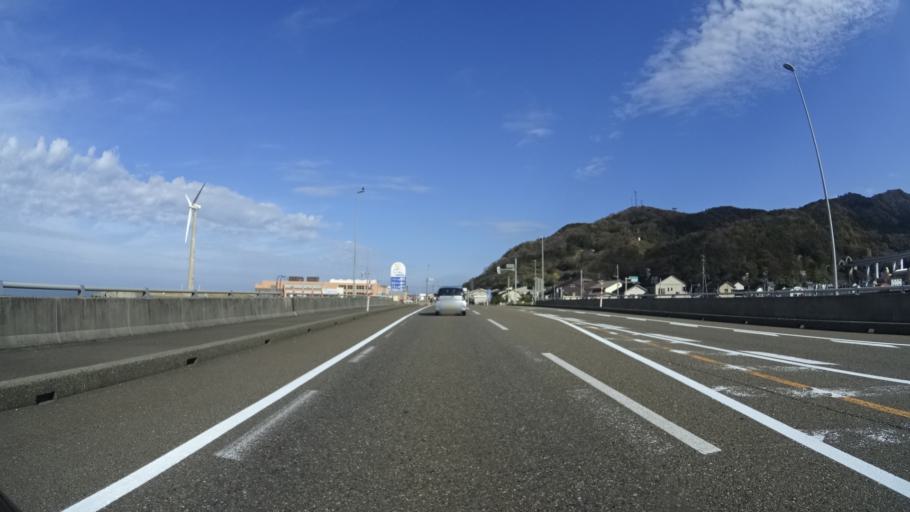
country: JP
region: Niigata
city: Joetsu
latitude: 37.1602
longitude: 138.0849
